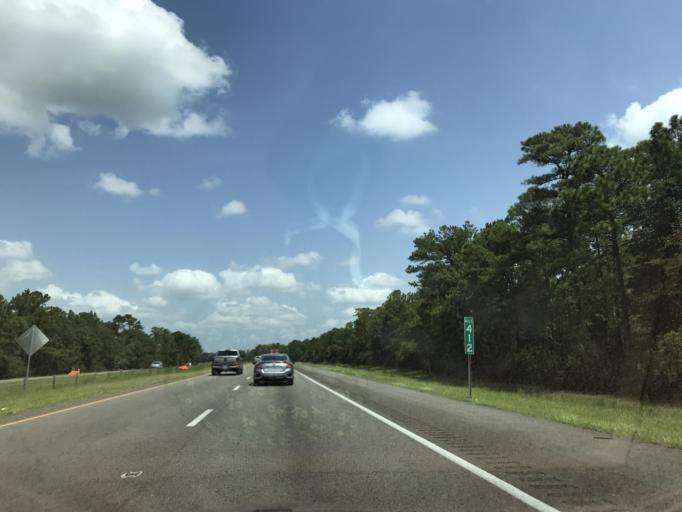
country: US
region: North Carolina
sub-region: New Hanover County
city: Castle Hayne
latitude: 34.3849
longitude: -77.8784
